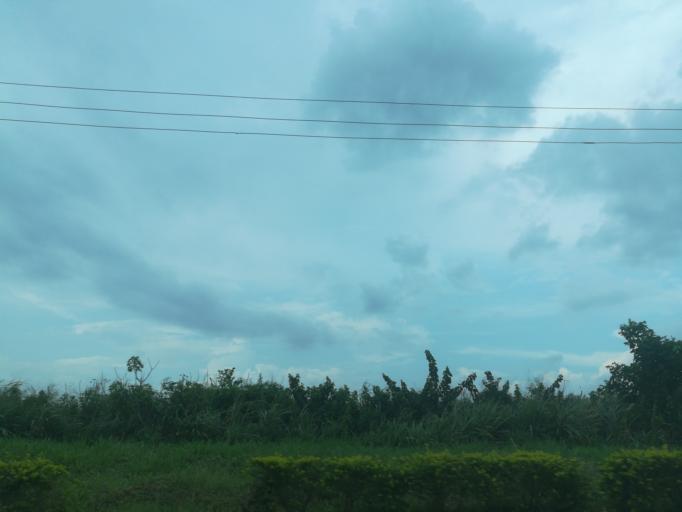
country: NG
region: Lagos
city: Ikorodu
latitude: 6.6357
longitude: 3.5278
